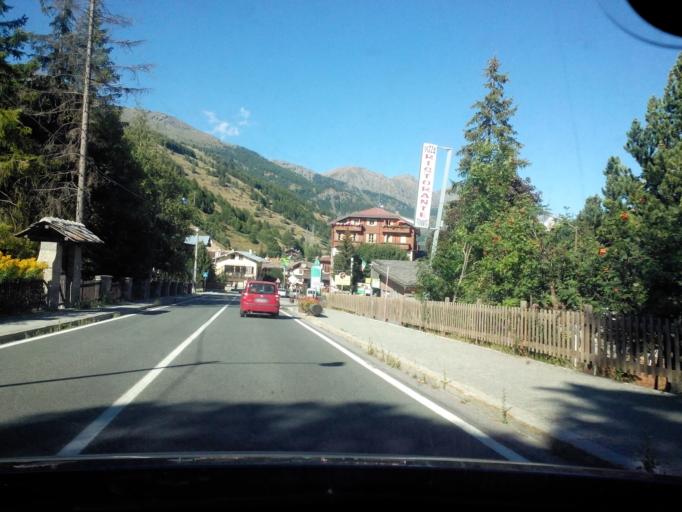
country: IT
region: Piedmont
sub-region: Provincia di Torino
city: Pragelato-Rua
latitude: 45.0147
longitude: 6.9416
